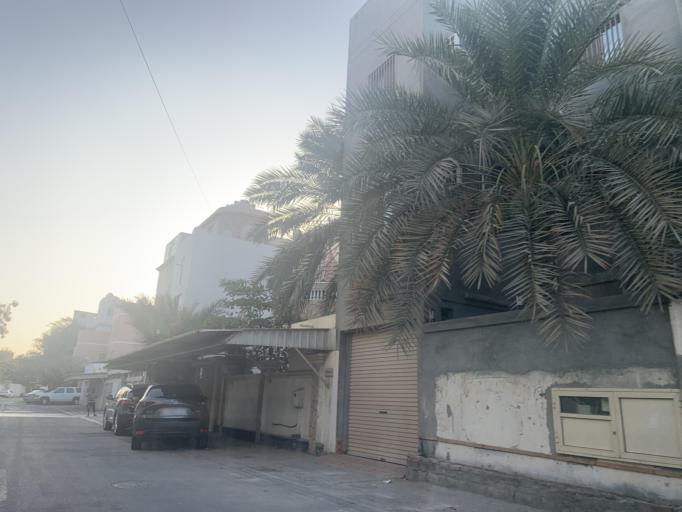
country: BH
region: Manama
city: Jidd Hafs
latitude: 26.2029
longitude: 50.5223
